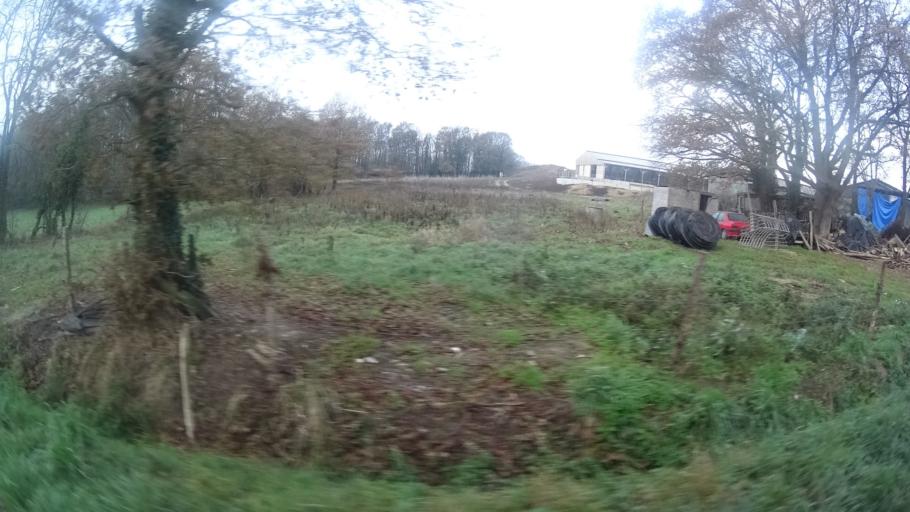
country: FR
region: Pays de la Loire
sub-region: Departement de la Loire-Atlantique
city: Saint-Nicolas-de-Redon
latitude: 47.6377
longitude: -2.0413
